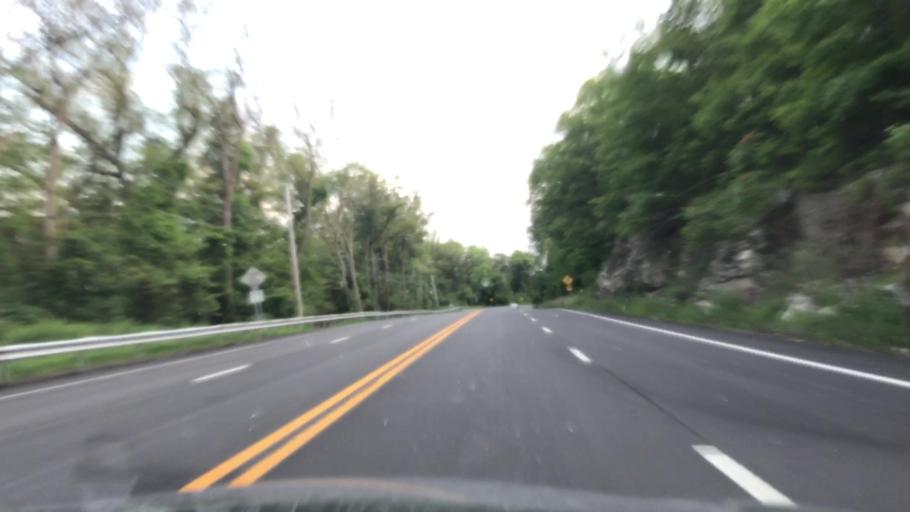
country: US
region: New York
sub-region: Orange County
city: Harriman
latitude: 41.2615
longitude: -74.1606
